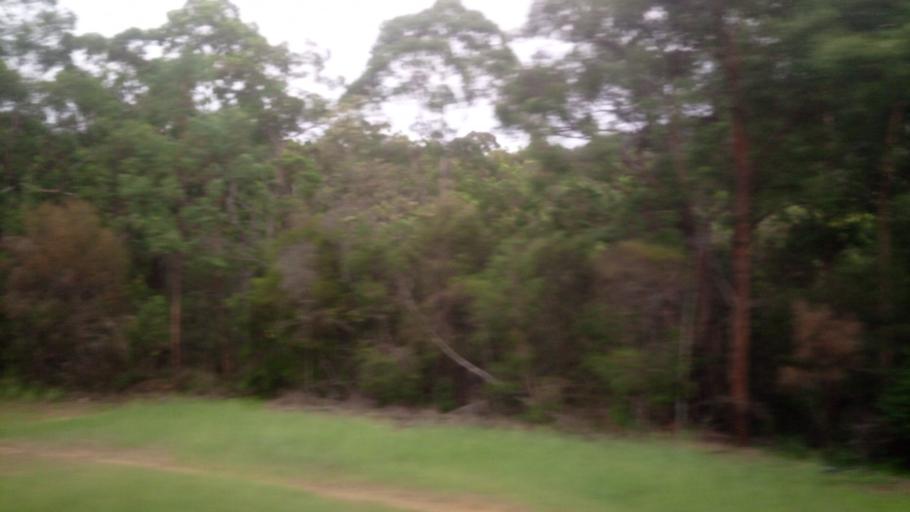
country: AU
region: New South Wales
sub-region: Penrith Municipality
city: Emu Heights
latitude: -33.7495
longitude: 150.6440
